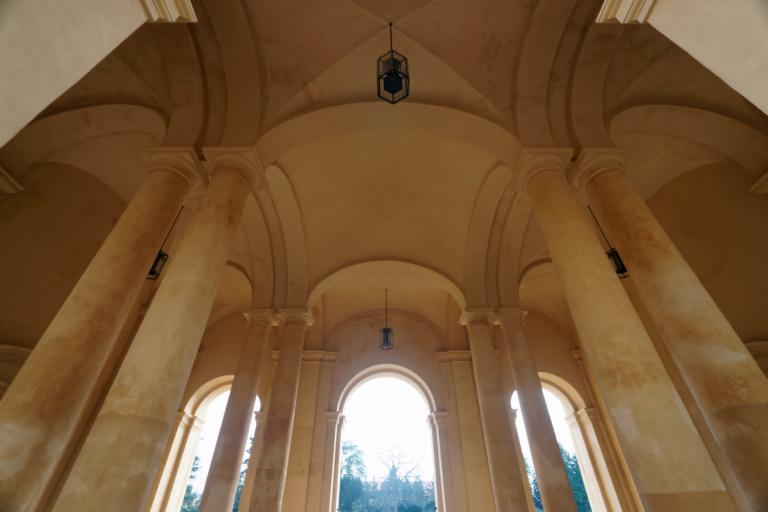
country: CZ
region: South Moravian
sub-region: Okres Breclav
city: Lednice
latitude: 48.8022
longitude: 16.8043
